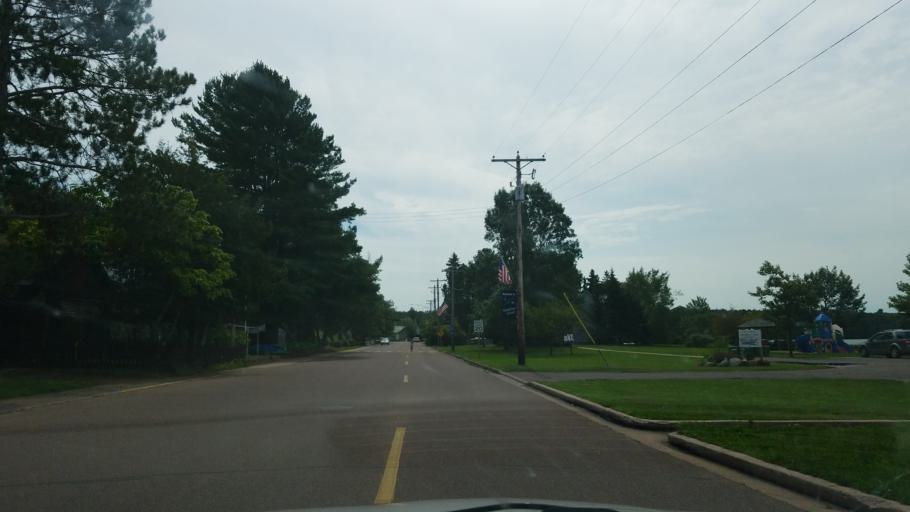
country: US
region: Wisconsin
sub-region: Bayfield County
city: Washburn
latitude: 46.7756
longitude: -90.7837
